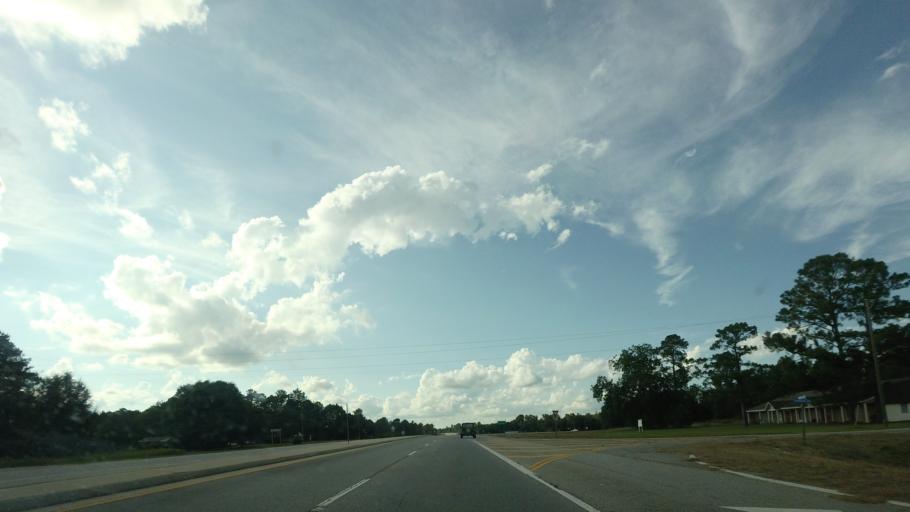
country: US
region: Georgia
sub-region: Pulaski County
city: Hawkinsville
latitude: 32.3024
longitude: -83.4968
